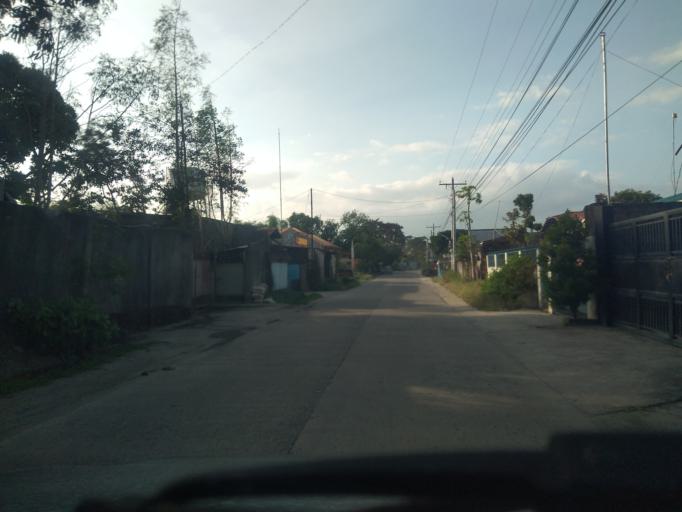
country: PH
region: Central Luzon
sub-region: Province of Pampanga
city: Malino
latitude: 15.1035
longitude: 120.6762
